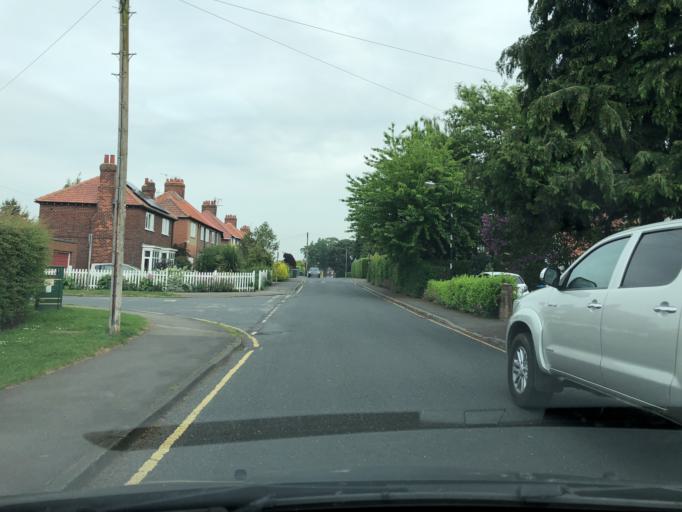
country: GB
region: England
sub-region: North Yorkshire
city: Northallerton
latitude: 54.3305
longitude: -1.4467
